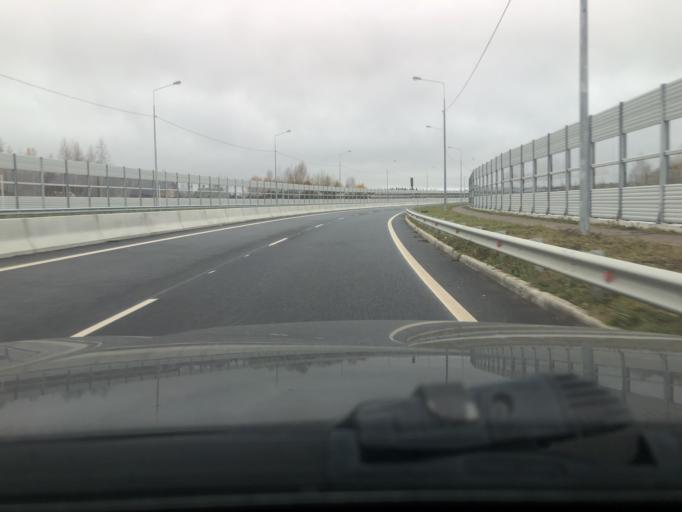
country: RU
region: Moskovskaya
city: Semkhoz
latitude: 56.3202
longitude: 38.0790
